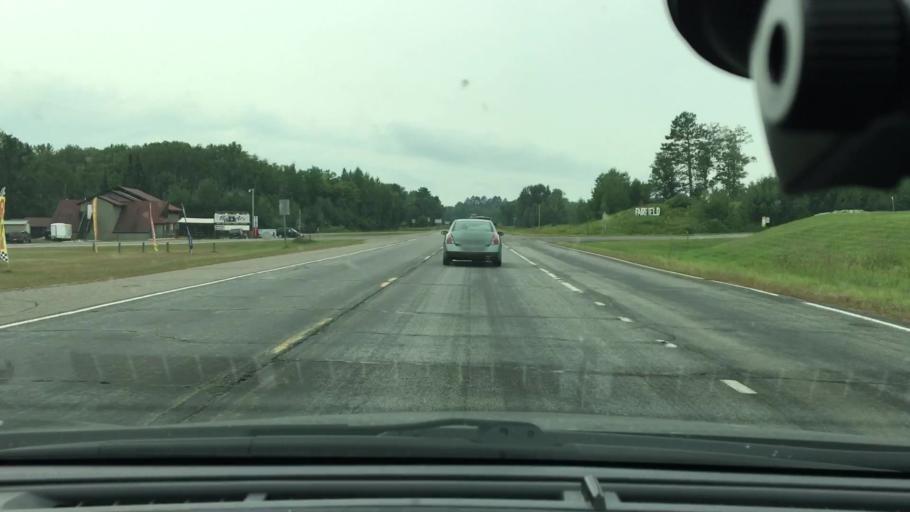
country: US
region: Minnesota
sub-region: Crow Wing County
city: Cross Lake
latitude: 46.6631
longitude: -93.9535
